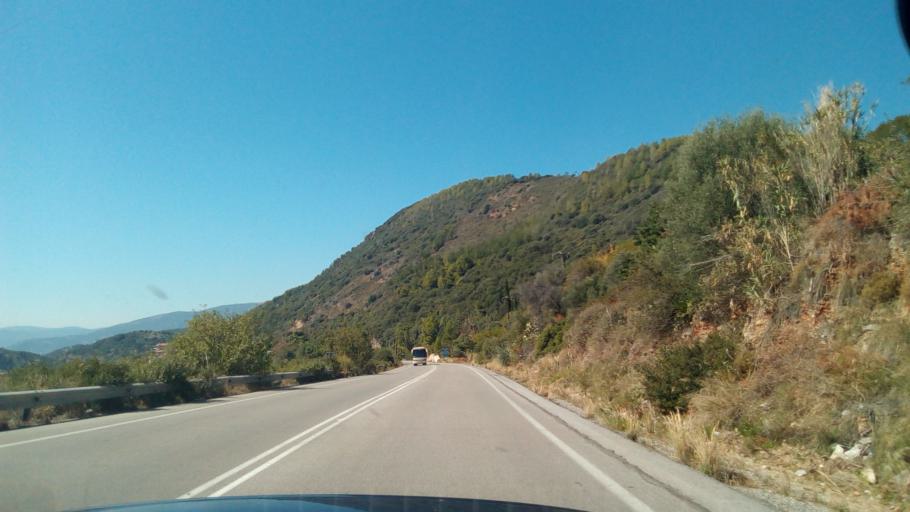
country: GR
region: West Greece
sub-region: Nomos Achaias
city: Kamarai
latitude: 38.4073
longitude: 21.9505
